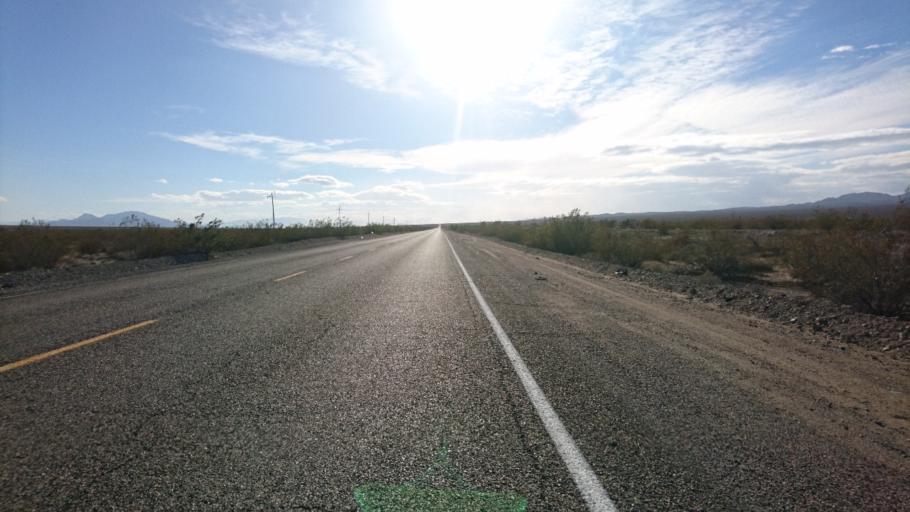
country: US
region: California
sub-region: San Bernardino County
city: Needles
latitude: 34.6993
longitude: -115.2996
